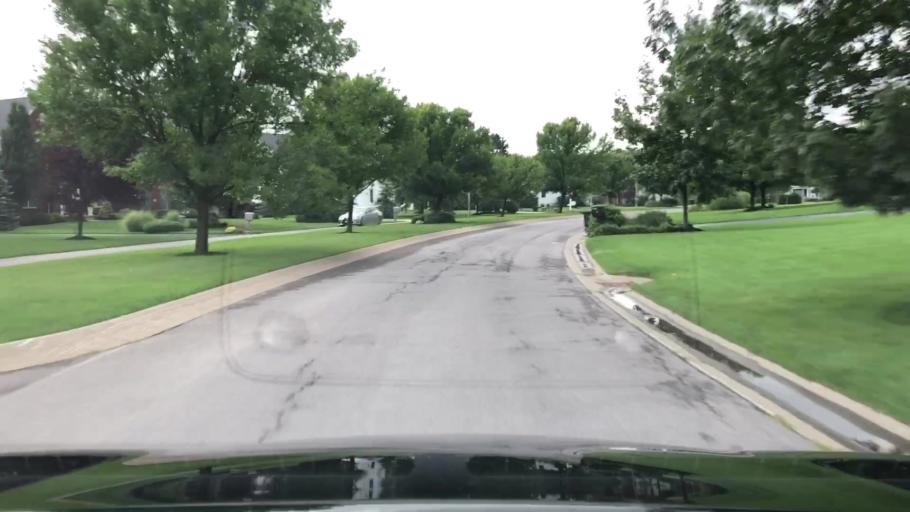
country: US
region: New York
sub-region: Erie County
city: Orchard Park
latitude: 42.7536
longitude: -78.7187
